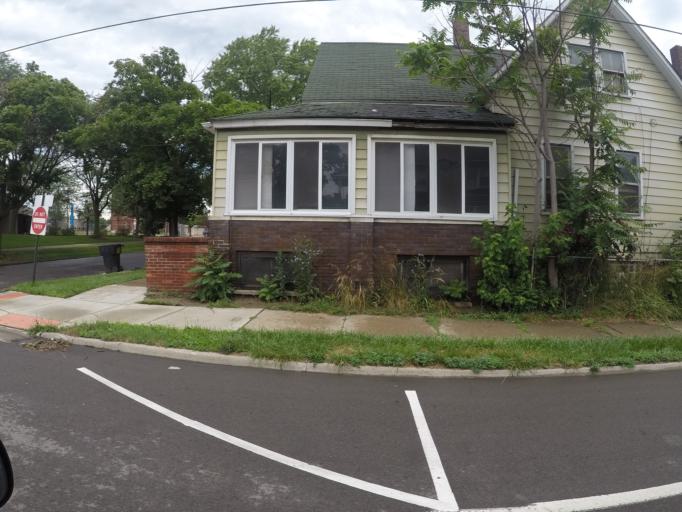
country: US
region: Michigan
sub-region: Wayne County
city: Hamtramck
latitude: 42.3750
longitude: -83.0157
